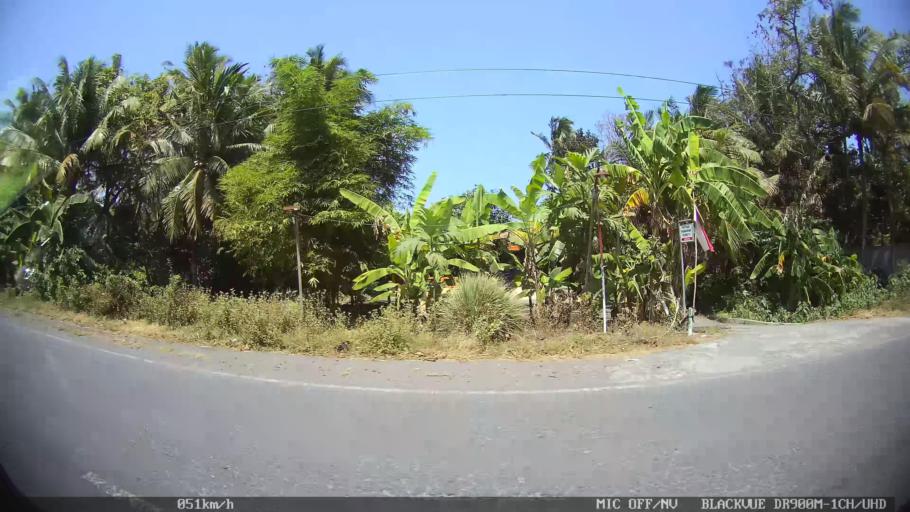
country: ID
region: Daerah Istimewa Yogyakarta
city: Srandakan
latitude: -7.9331
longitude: 110.1434
